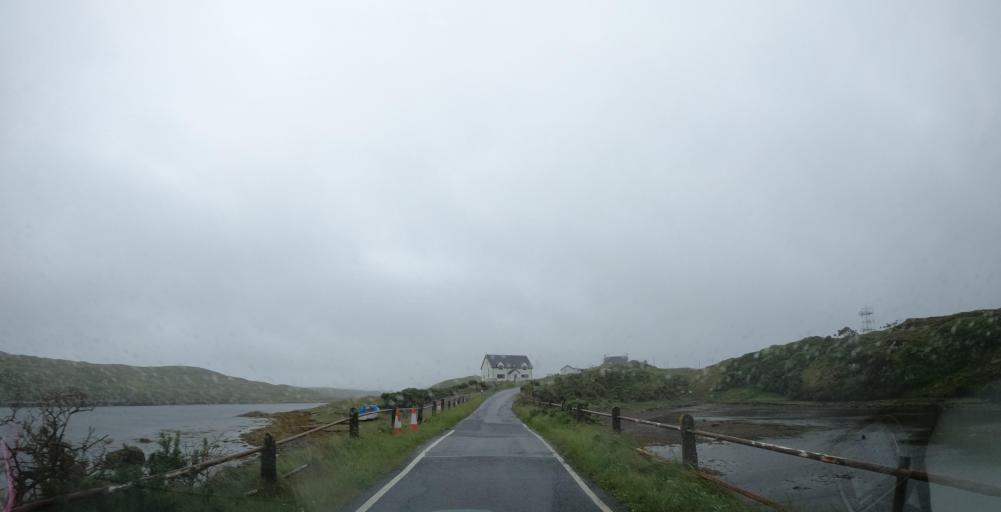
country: GB
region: Scotland
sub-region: Eilean Siar
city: Barra
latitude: 56.9903
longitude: -7.4200
